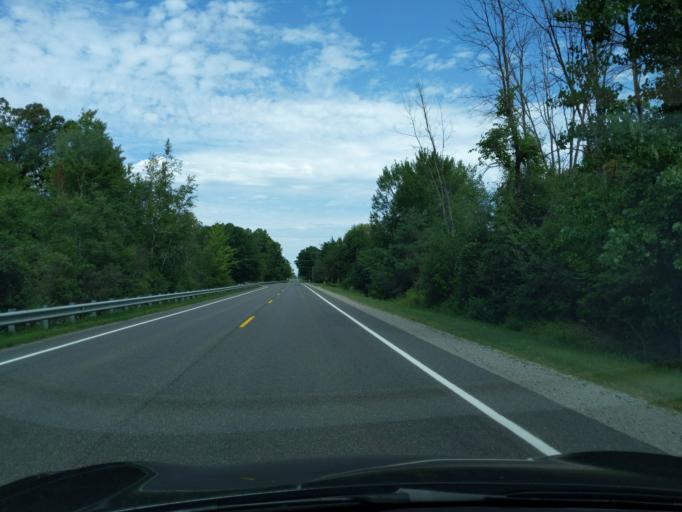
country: US
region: Michigan
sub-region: Midland County
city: Midland
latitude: 43.5519
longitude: -84.3697
